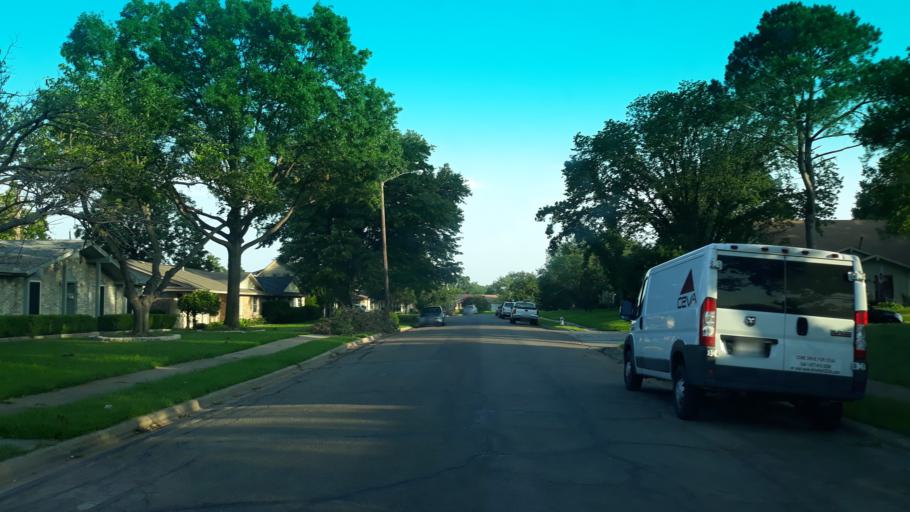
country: US
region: Texas
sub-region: Dallas County
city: Irving
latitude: 32.8526
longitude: -97.0054
